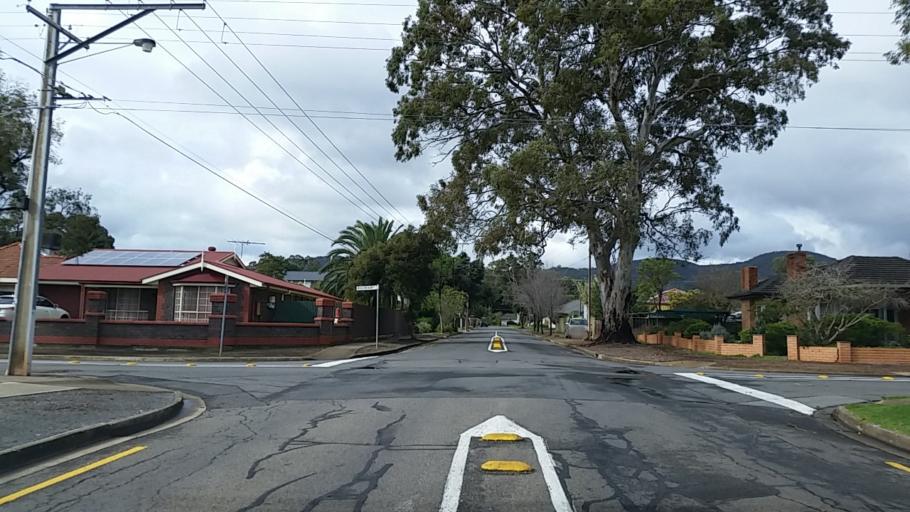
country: AU
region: South Australia
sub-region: Campbelltown
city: Campbelltown
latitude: -34.8922
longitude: 138.6789
